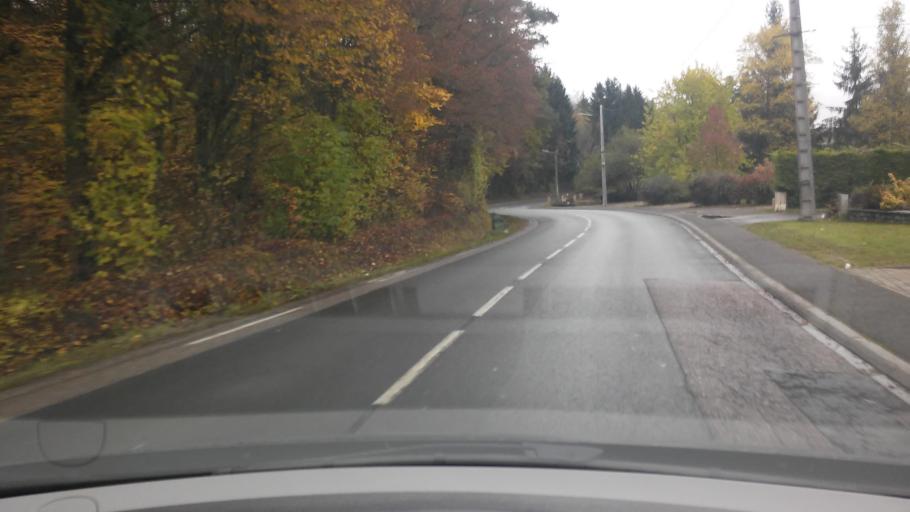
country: FR
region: Lorraine
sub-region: Departement de la Moselle
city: Kedange-sur-Canner
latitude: 49.3050
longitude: 6.3379
